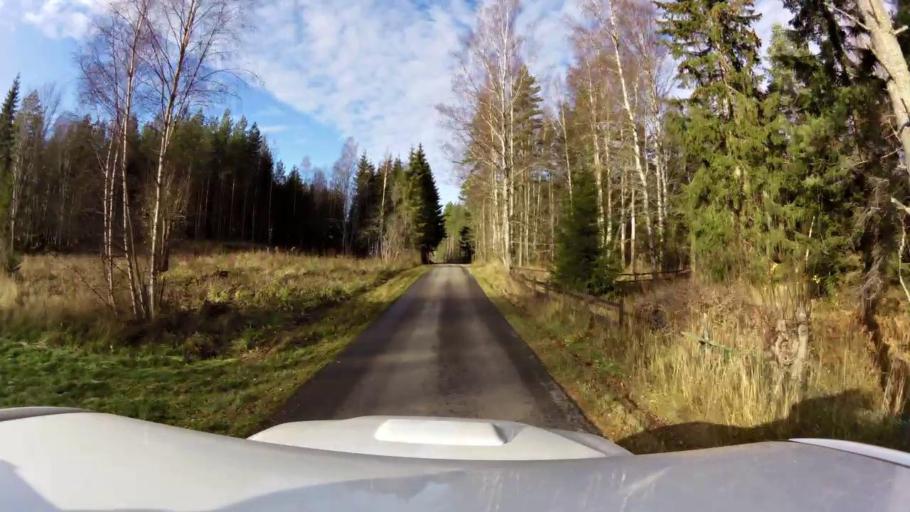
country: SE
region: OEstergoetland
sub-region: Linkopings Kommun
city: Sturefors
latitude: 58.2611
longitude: 15.6894
